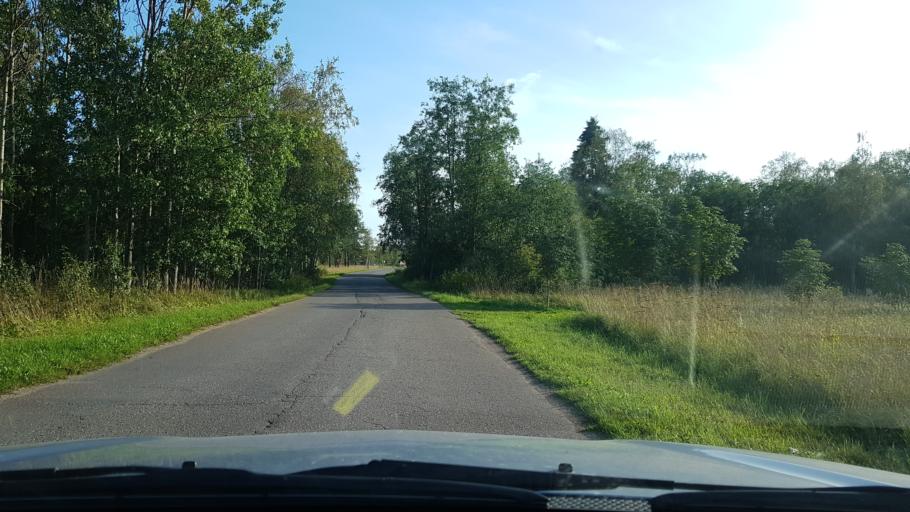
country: EE
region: Ida-Virumaa
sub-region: Narva-Joesuu linn
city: Narva-Joesuu
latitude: 59.3860
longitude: 28.0886
